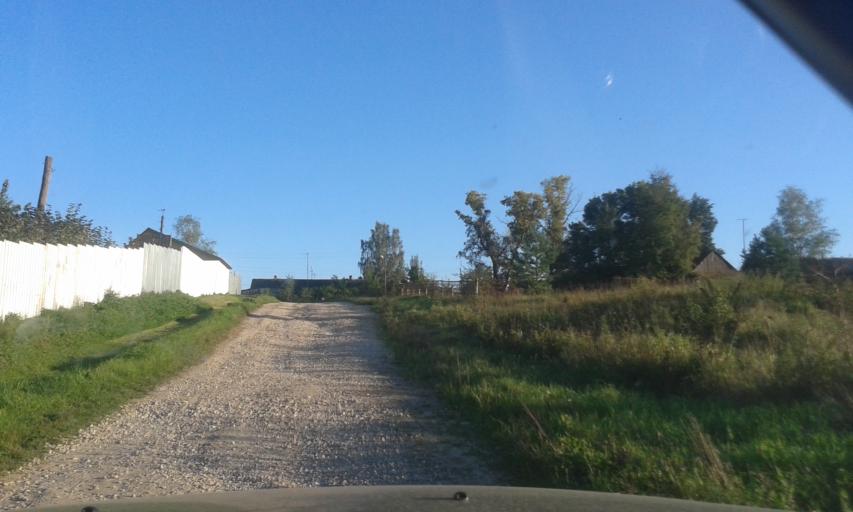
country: RU
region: Tula
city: Dubna
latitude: 54.1358
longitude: 37.1519
